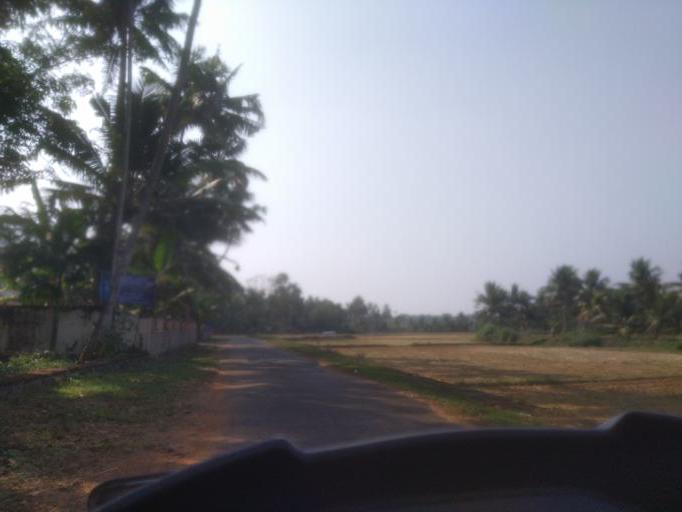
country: IN
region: Kerala
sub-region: Ernakulam
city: Piravam
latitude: 9.8779
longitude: 76.5532
